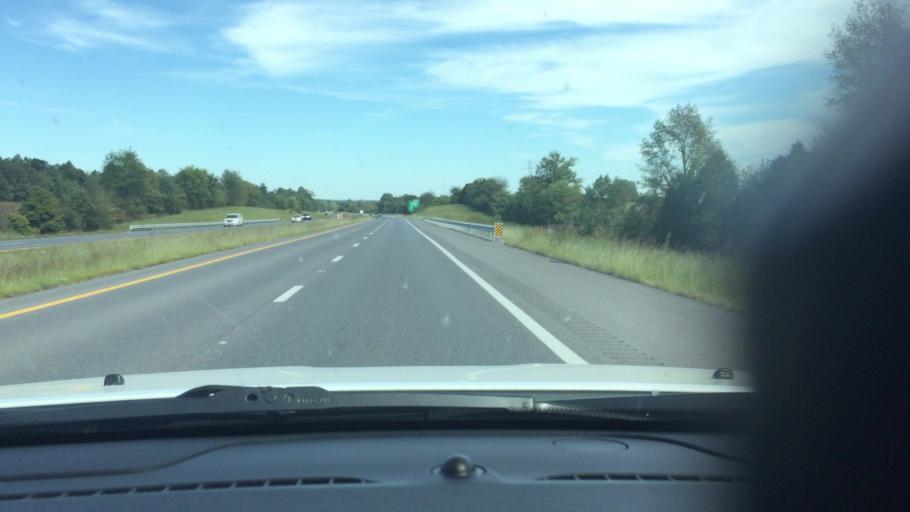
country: US
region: Kentucky
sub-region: Caldwell County
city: Princeton
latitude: 37.1124
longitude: -87.9383
